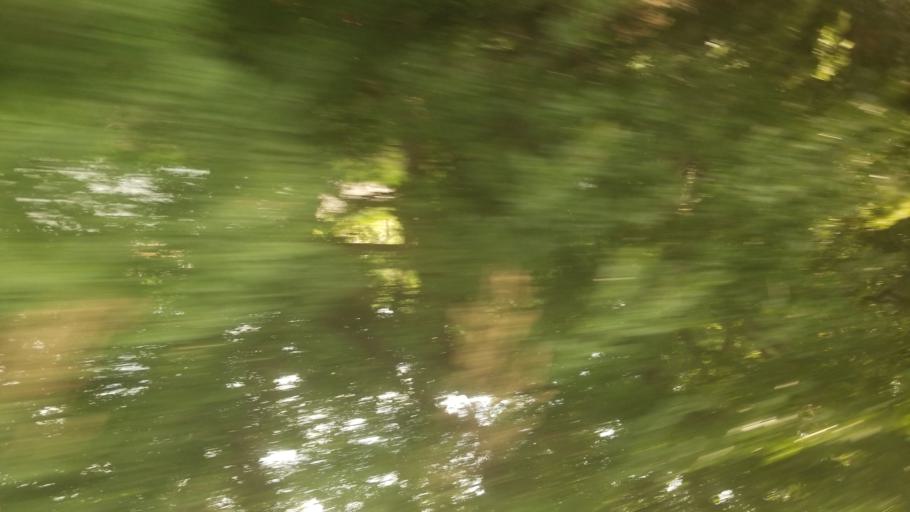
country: US
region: Kansas
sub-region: Douglas County
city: Eudora
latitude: 38.9483
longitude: -95.1063
